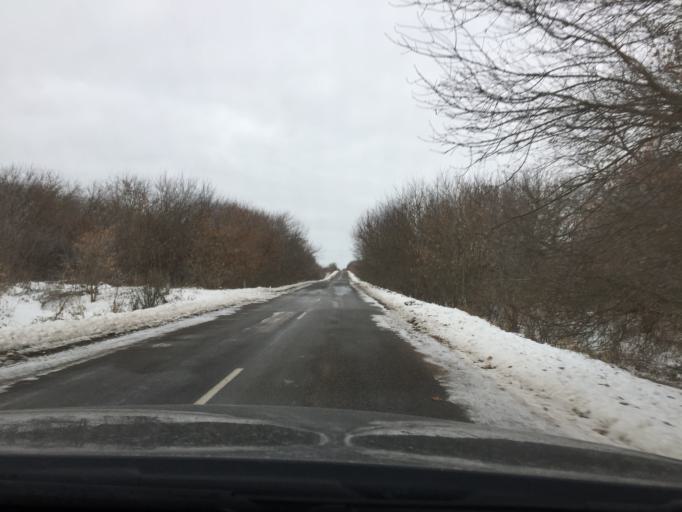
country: RU
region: Tula
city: Teploye
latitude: 53.7937
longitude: 37.6032
